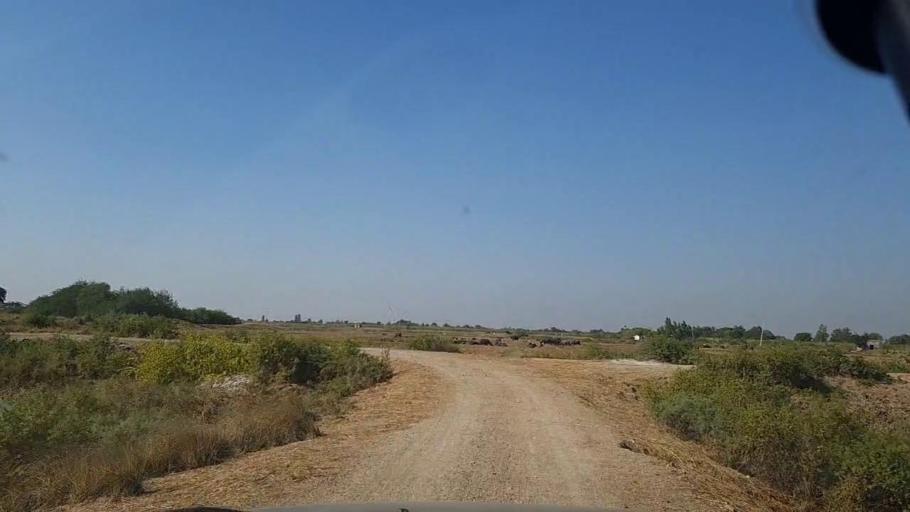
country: PK
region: Sindh
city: Chuhar Jamali
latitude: 24.5762
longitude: 68.0399
